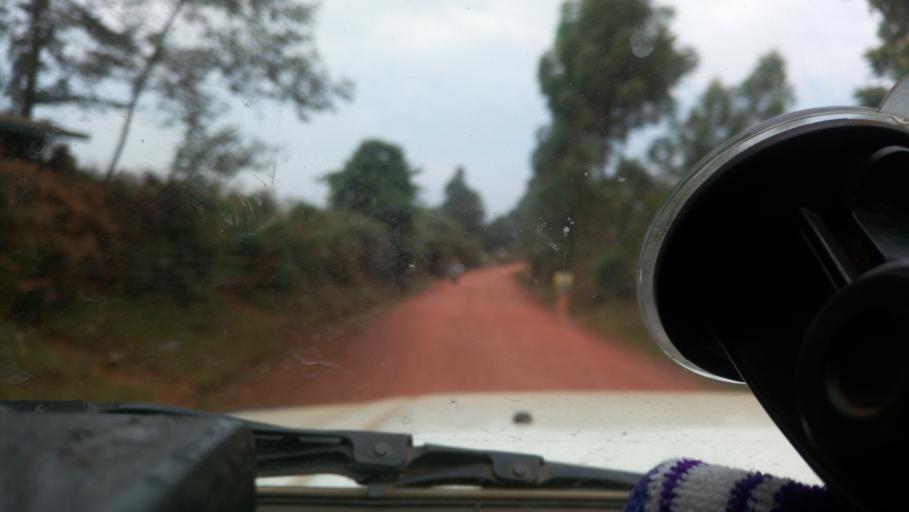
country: KE
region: Kericho
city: Litein
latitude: -0.6118
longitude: 35.2223
